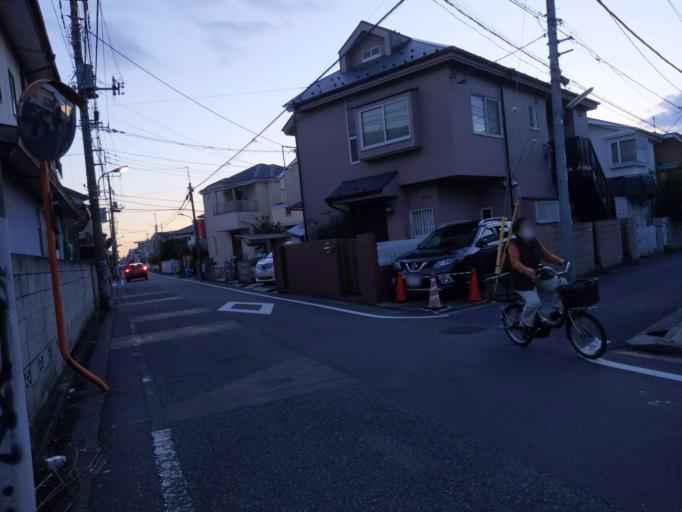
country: JP
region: Tokyo
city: Tokyo
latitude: 35.6609
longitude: 139.6273
